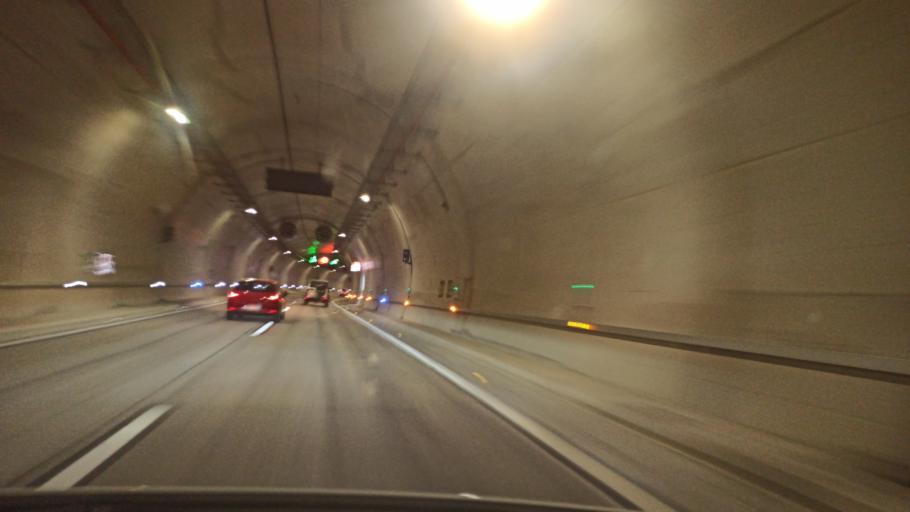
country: ES
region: Catalonia
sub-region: Provincia de Barcelona
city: Vallirana
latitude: 41.3811
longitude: 1.9330
